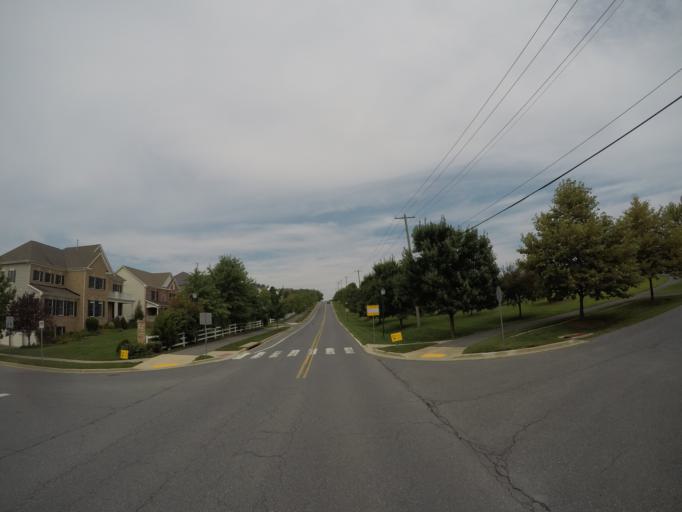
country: US
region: Maryland
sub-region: Montgomery County
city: Clarksburg
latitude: 39.2381
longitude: -77.2514
